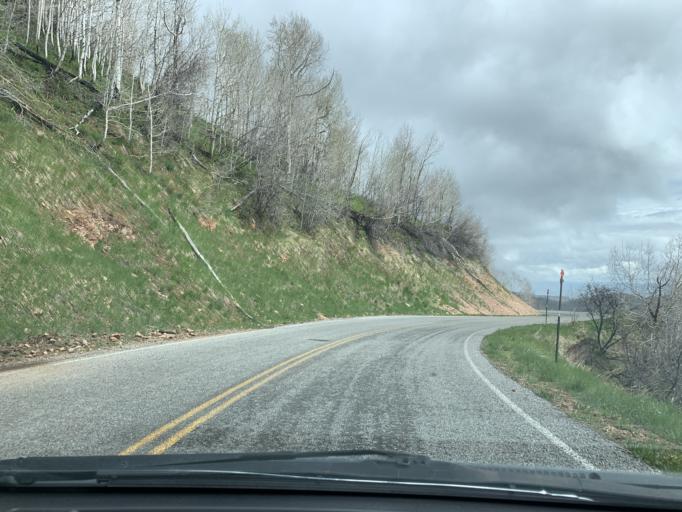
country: US
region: Utah
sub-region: Utah County
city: Elk Ridge
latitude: 39.8730
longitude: -111.6850
